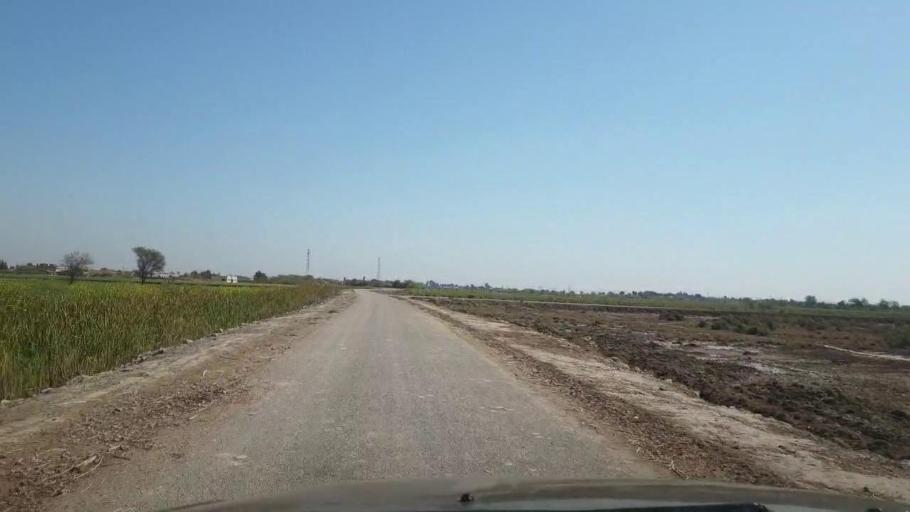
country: PK
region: Sindh
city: Mirpur Khas
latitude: 25.5693
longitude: 69.0573
